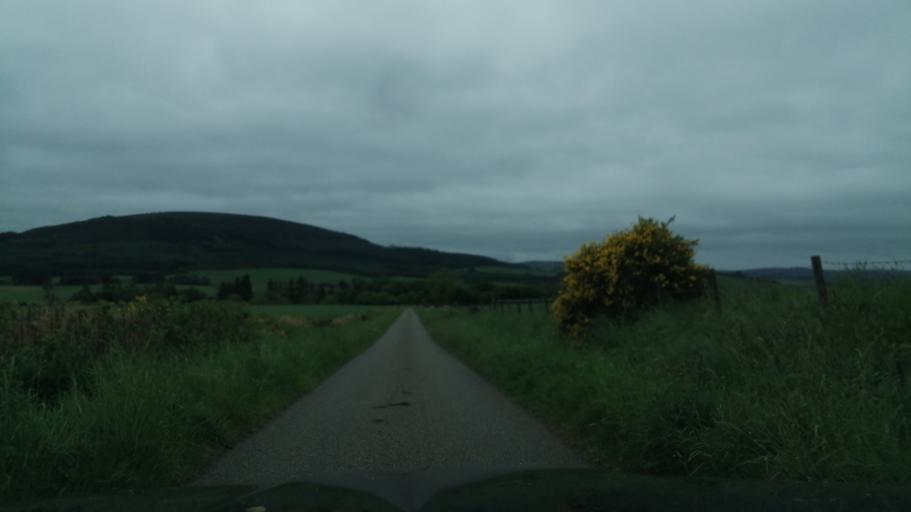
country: GB
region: Scotland
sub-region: Moray
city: Keith
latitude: 57.5561
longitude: -2.8673
